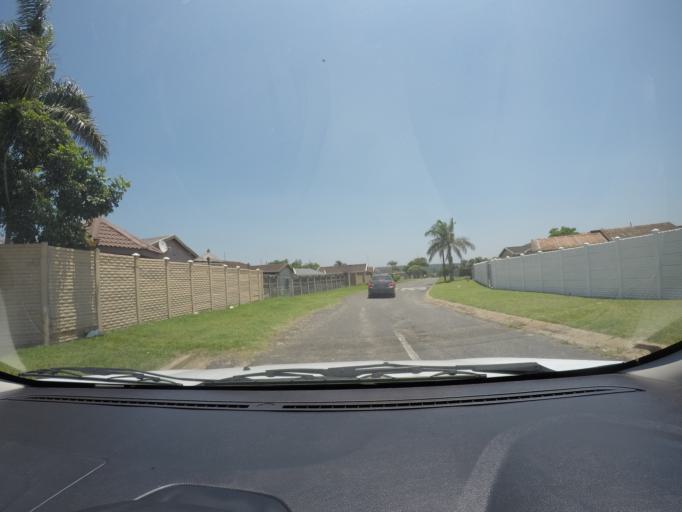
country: ZA
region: KwaZulu-Natal
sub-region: uThungulu District Municipality
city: eSikhawini
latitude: -28.8781
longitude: 31.9052
